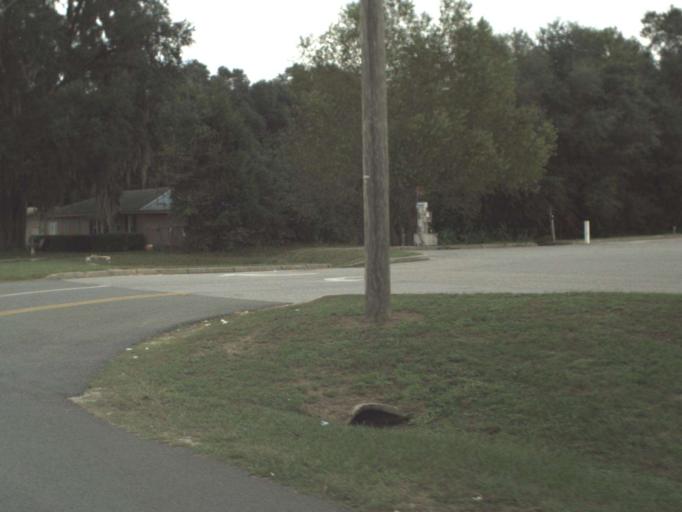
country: US
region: Florida
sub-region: Jackson County
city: Marianna
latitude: 30.7109
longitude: -85.1852
